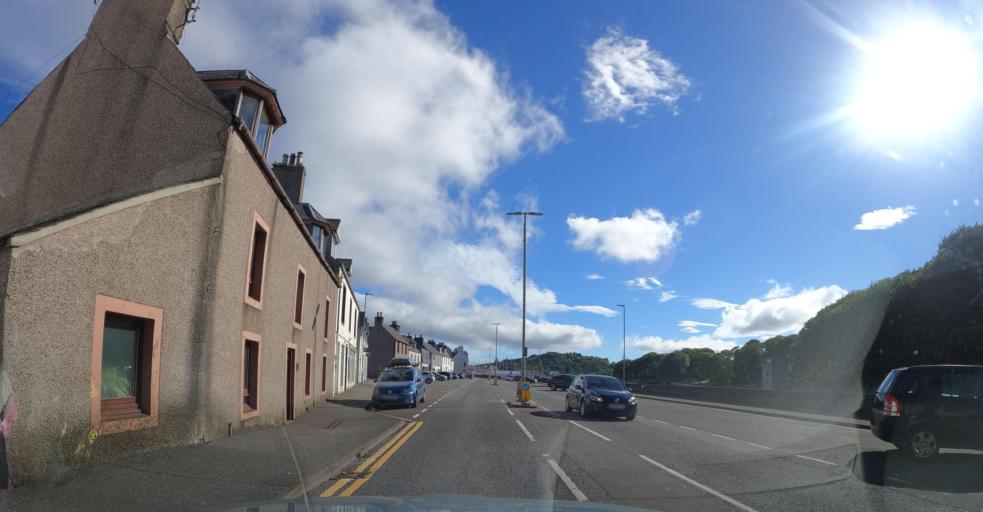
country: GB
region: Scotland
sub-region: Eilean Siar
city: Stornoway
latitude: 58.2125
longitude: -6.3877
